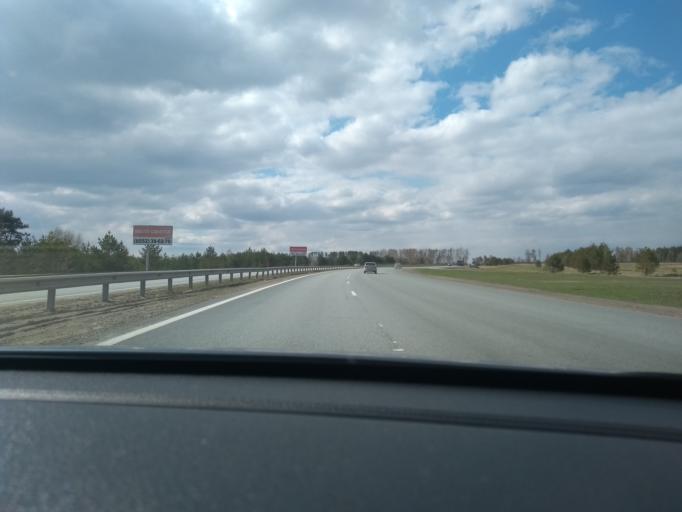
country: RU
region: Tatarstan
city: Yelabuga
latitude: 55.7826
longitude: 52.1753
